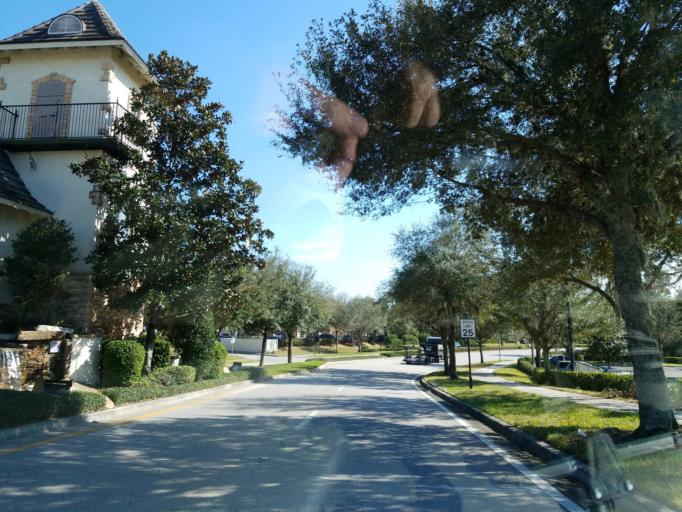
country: US
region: Florida
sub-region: Hillsborough County
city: Fish Hawk
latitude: 27.8541
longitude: -82.2072
